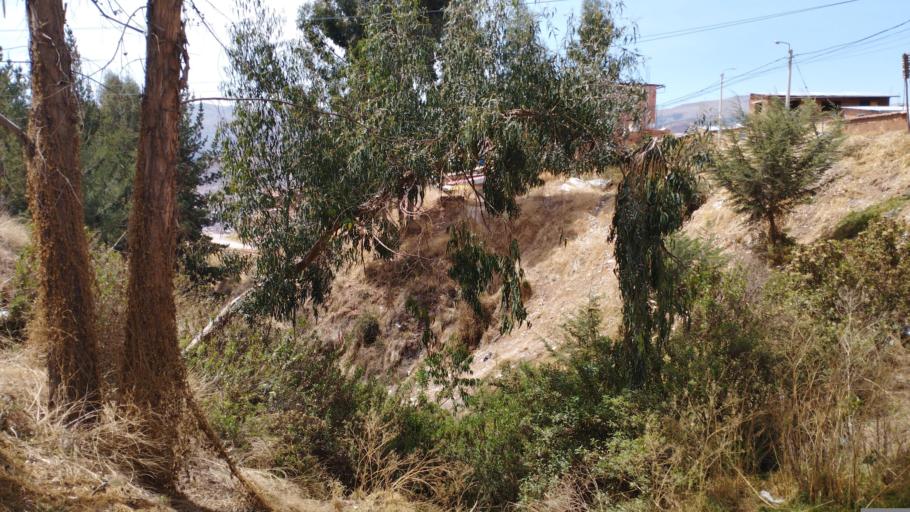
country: PE
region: Cusco
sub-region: Provincia de Cusco
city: Cusco
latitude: -13.5228
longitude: -71.9220
